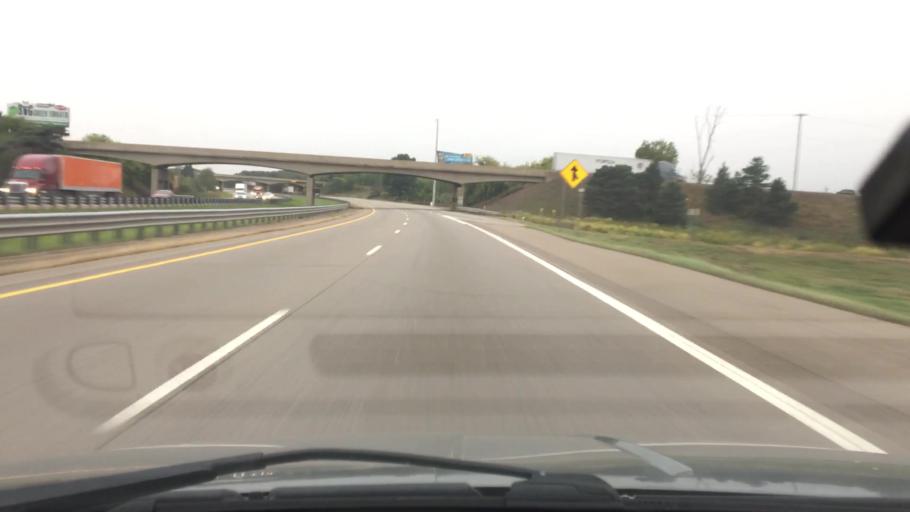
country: US
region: Michigan
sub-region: Calhoun County
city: Brownlee Park
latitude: 42.3001
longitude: -85.0796
